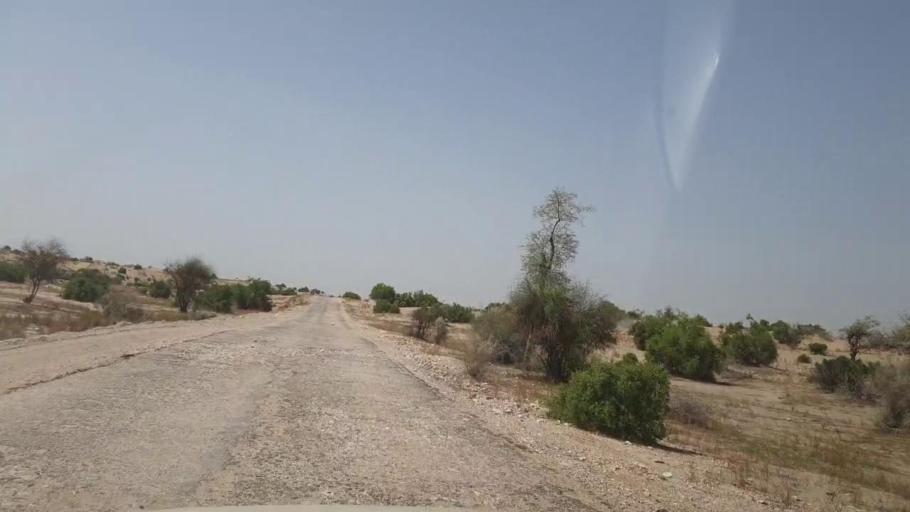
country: PK
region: Sindh
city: Khanpur
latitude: 27.3723
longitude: 69.3187
